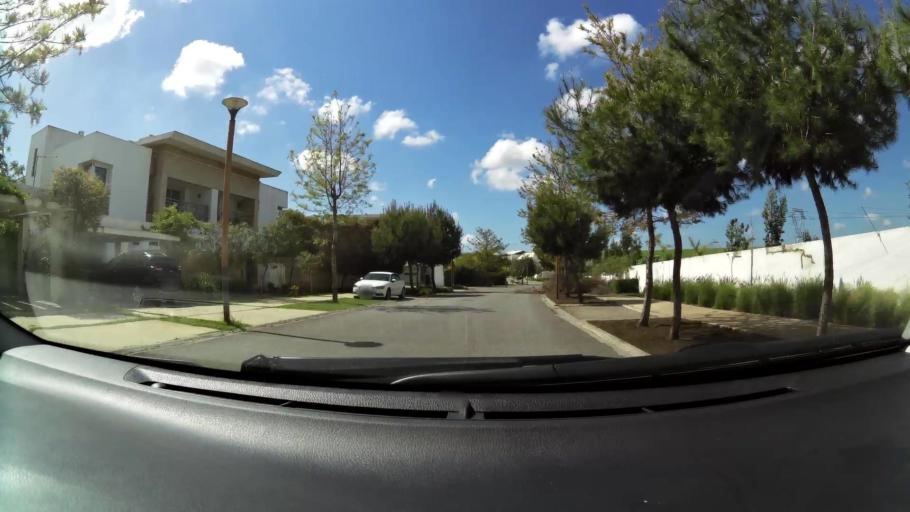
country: MA
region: Grand Casablanca
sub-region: Nouaceur
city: Bouskoura
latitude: 33.4915
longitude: -7.5910
